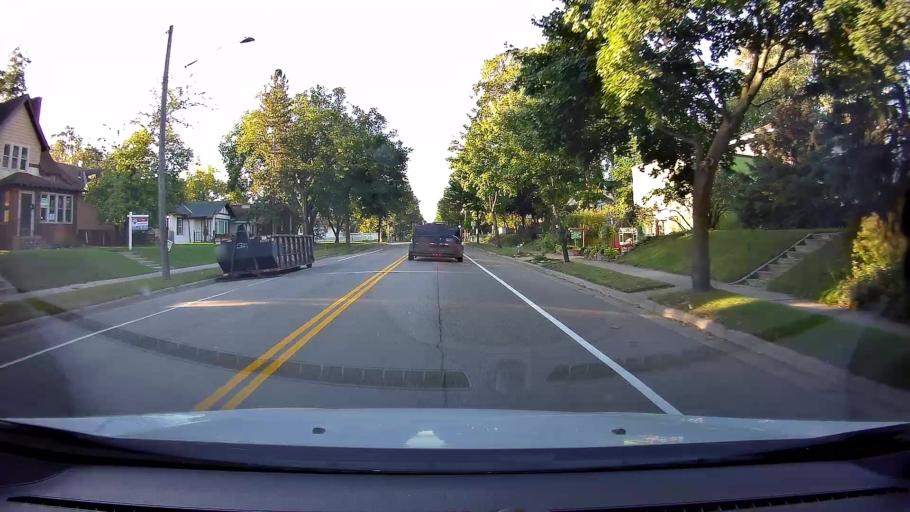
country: US
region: Minnesota
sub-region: Hennepin County
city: Minneapolis
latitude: 44.9313
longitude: -93.2474
